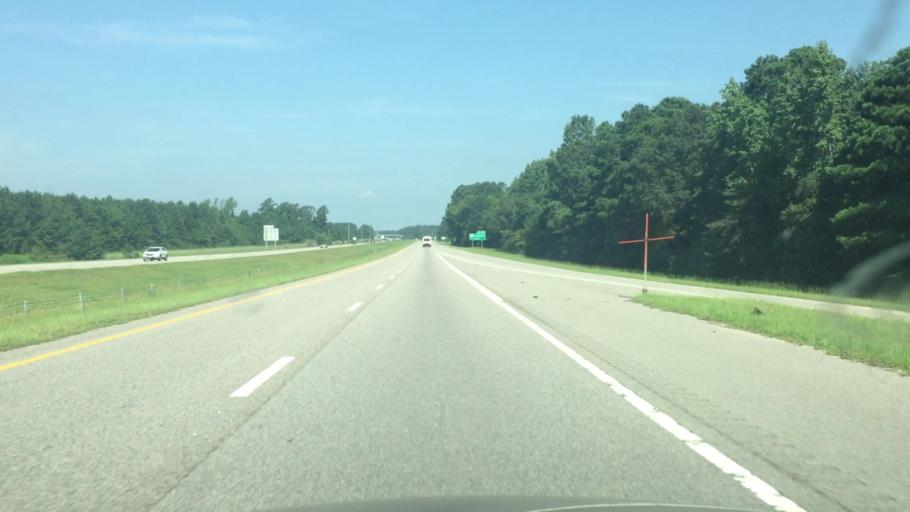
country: US
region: North Carolina
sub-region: Robeson County
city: Lumberton
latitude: 34.5811
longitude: -79.0505
